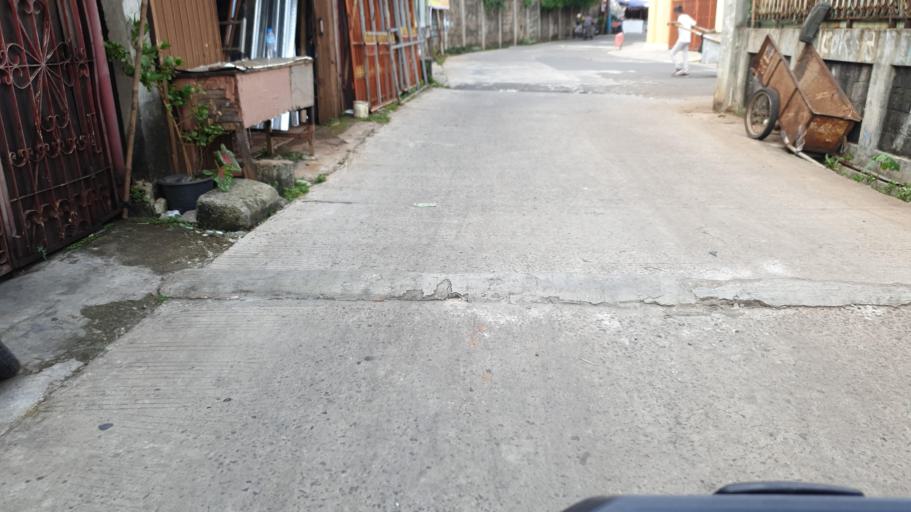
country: ID
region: West Java
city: Depok
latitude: -6.3665
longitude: 106.8474
